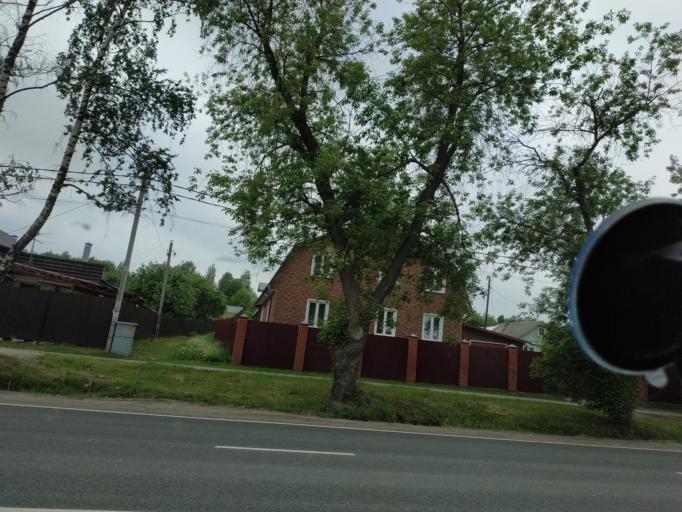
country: RU
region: Moskovskaya
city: Ostrovtsy
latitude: 55.5565
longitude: 38.0560
